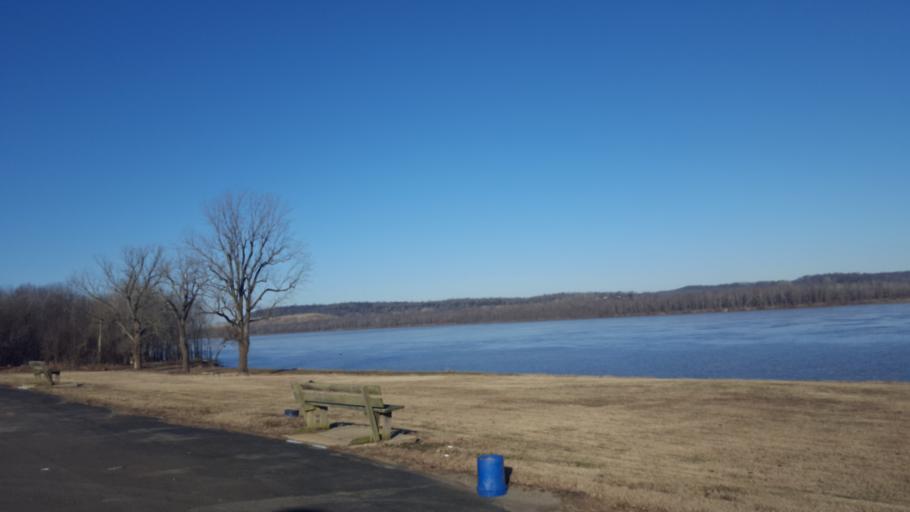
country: US
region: Kentucky
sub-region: Crittenden County
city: Marion
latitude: 37.4662
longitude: -88.0928
